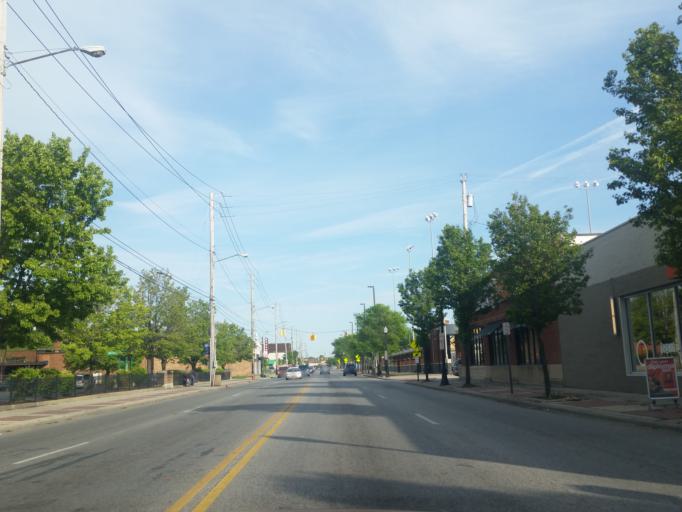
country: US
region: Ohio
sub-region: Cuyahoga County
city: Newburgh Heights
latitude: 41.4657
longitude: -81.6499
